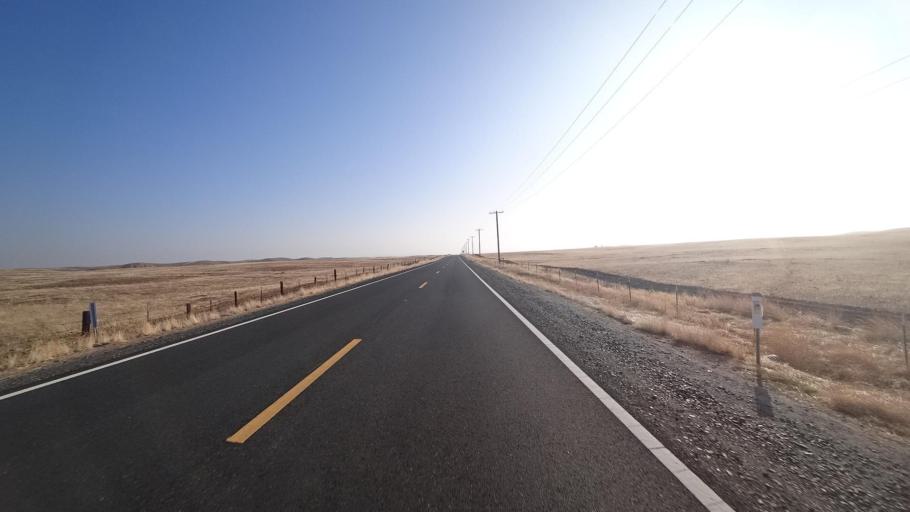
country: US
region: California
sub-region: Tulare County
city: Richgrove
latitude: 35.7620
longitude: -119.0480
